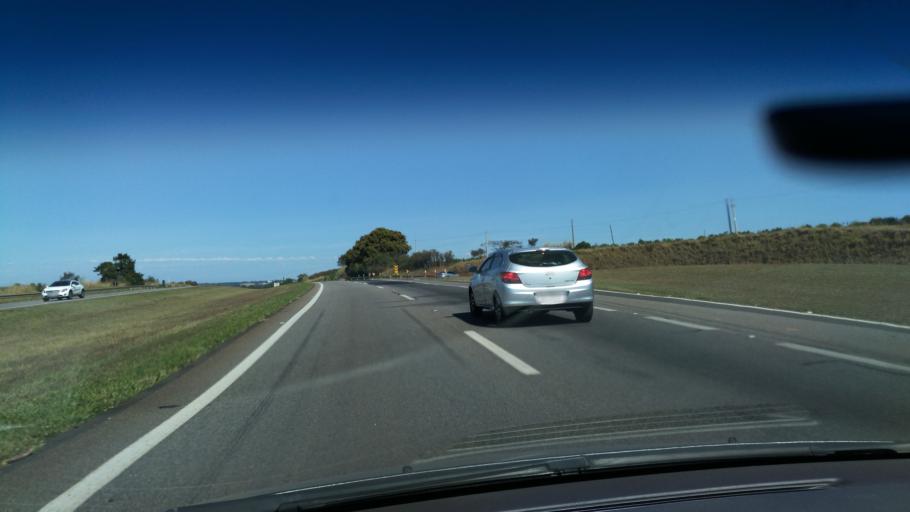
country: BR
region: Sao Paulo
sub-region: Santo Antonio De Posse
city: Santo Antonio de Posse
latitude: -22.5468
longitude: -46.9988
